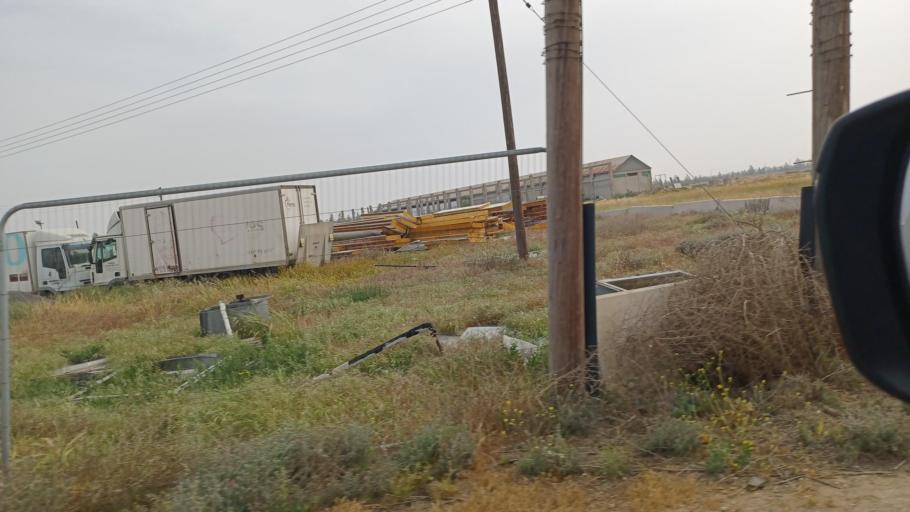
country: CY
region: Lefkosia
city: Kokkinotrimithia
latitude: 35.1571
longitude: 33.2155
